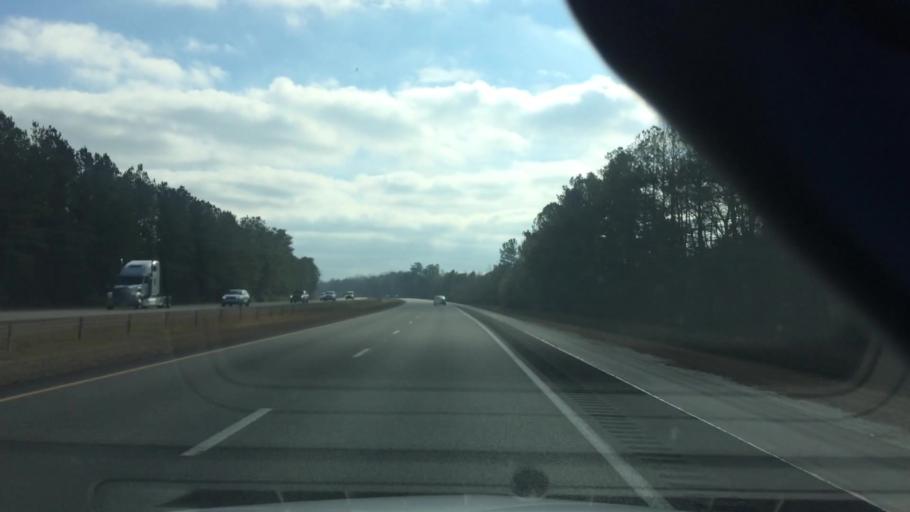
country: US
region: North Carolina
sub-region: Pender County
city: Rocky Point
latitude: 34.4664
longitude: -77.8802
